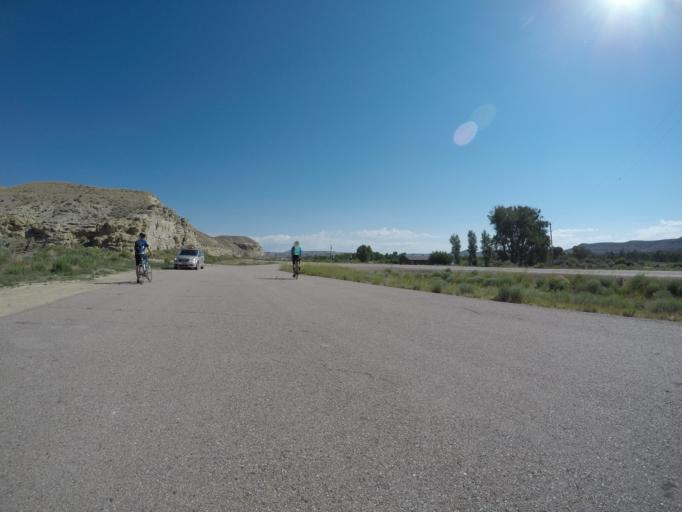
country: US
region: Wyoming
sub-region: Sublette County
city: Marbleton
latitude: 42.1767
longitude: -110.1872
